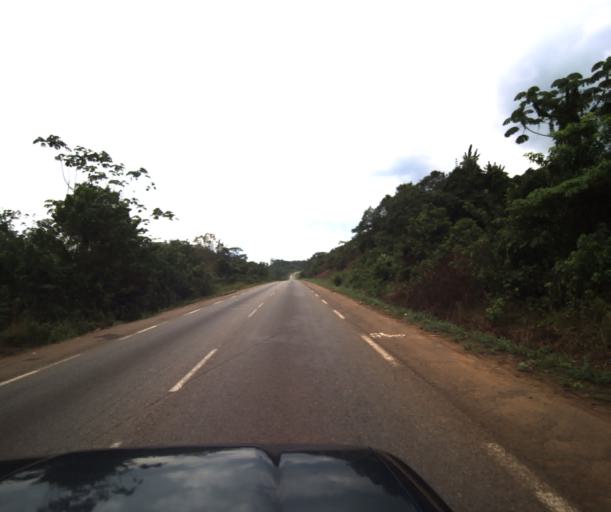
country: CM
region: Littoral
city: Edea
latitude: 3.8695
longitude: 10.0733
